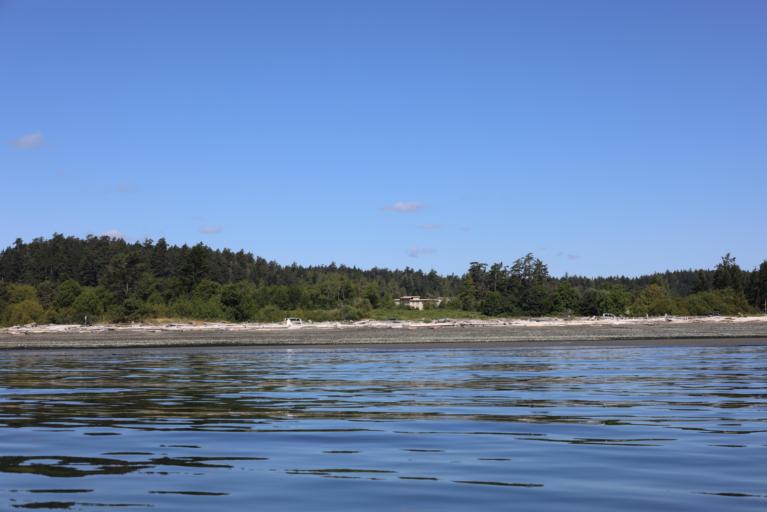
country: CA
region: British Columbia
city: Colwood
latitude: 48.4179
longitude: -123.4682
